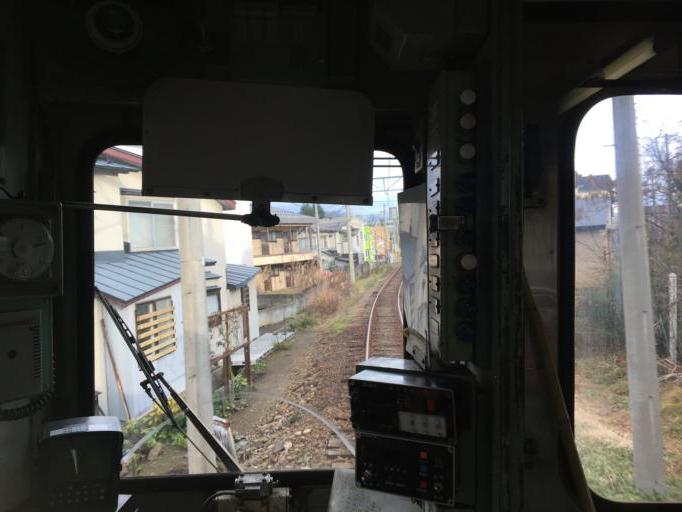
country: JP
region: Aomori
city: Hirosaki
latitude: 40.5915
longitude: 140.4682
